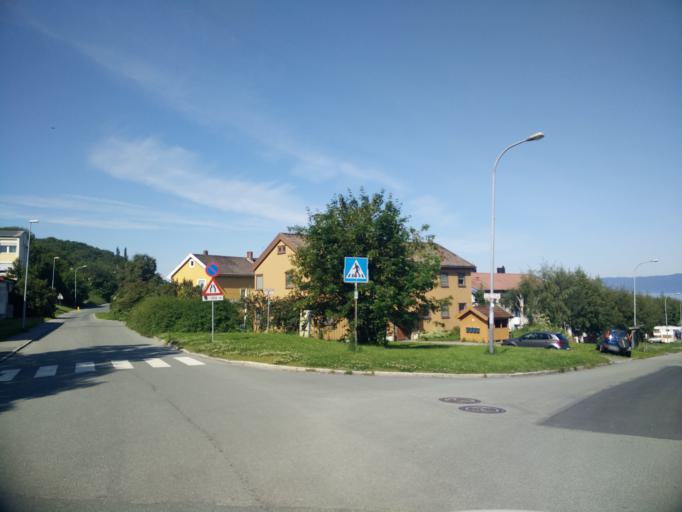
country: NO
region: Sor-Trondelag
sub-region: Trondheim
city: Trondheim
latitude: 63.4475
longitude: 10.4379
